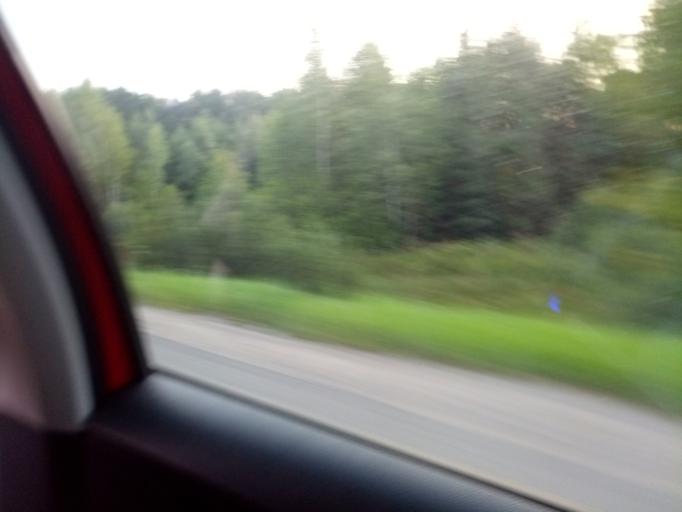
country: RU
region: Moskovskaya
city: Noginsk-9
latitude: 56.0607
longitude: 38.5533
